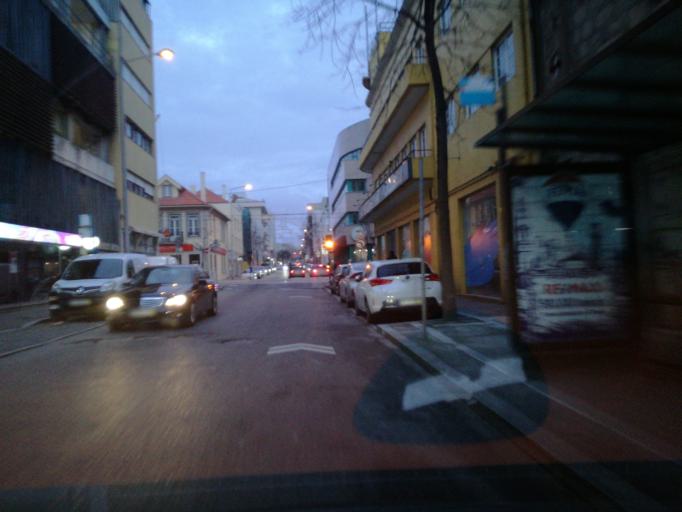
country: PT
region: Porto
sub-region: Matosinhos
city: Matosinhos
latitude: 41.1818
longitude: -8.6901
